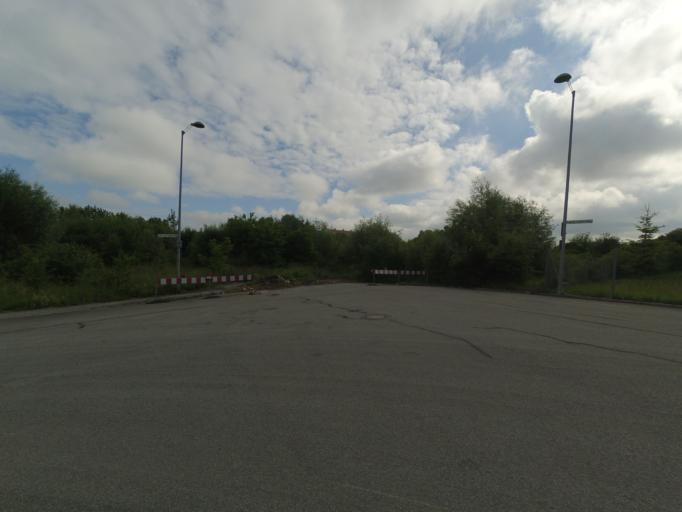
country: DE
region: Bavaria
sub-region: Lower Bavaria
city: Straubing
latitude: 48.8776
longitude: 12.5534
